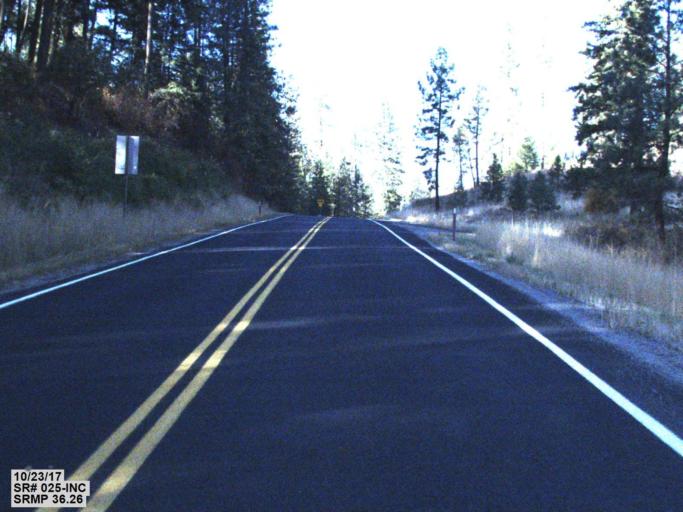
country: US
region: Washington
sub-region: Lincoln County
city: Davenport
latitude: 48.0519
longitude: -118.2221
